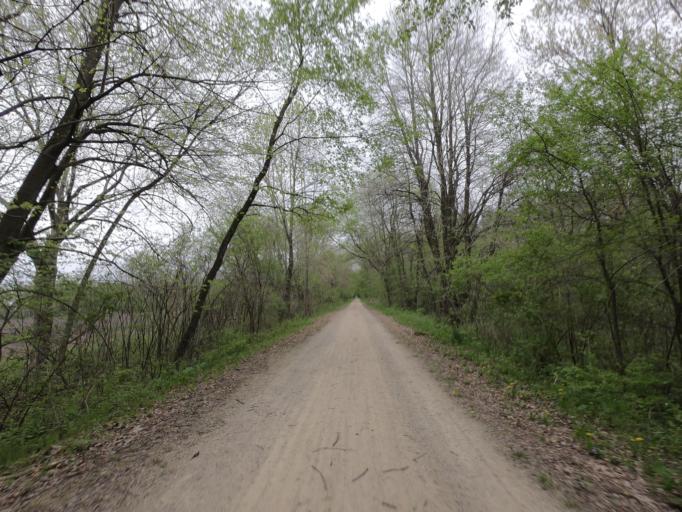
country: US
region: Wisconsin
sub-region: Jefferson County
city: Jefferson
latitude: 43.0404
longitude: -88.8391
